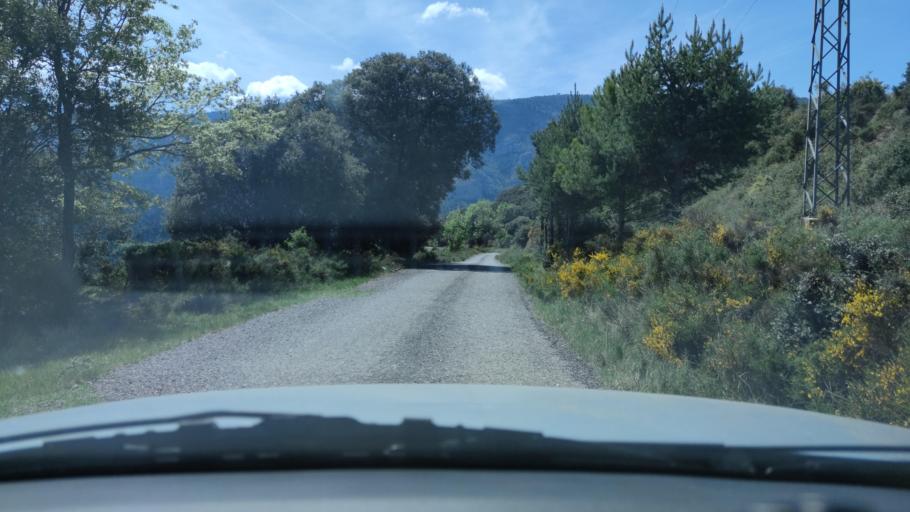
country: ES
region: Catalonia
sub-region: Provincia de Lleida
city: Sort
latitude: 42.3179
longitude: 1.0859
